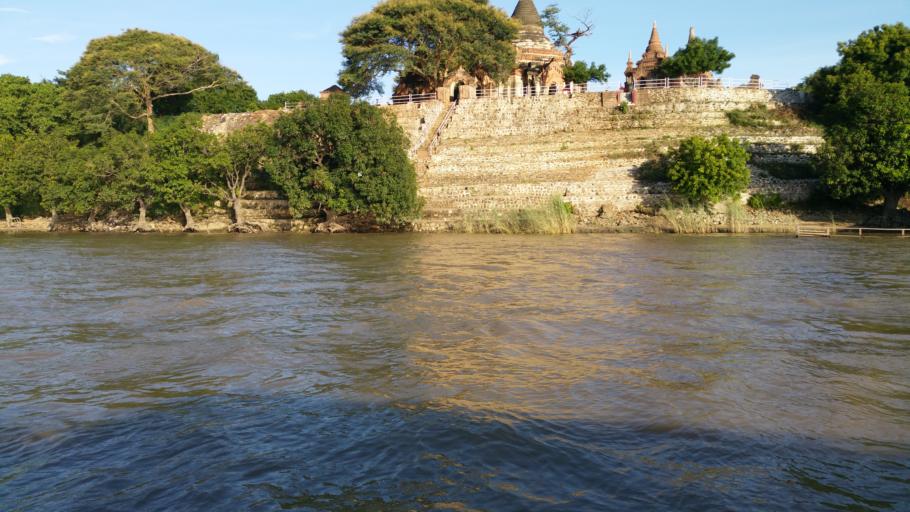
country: MM
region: Magway
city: Pakokku
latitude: 21.1817
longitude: 94.8626
